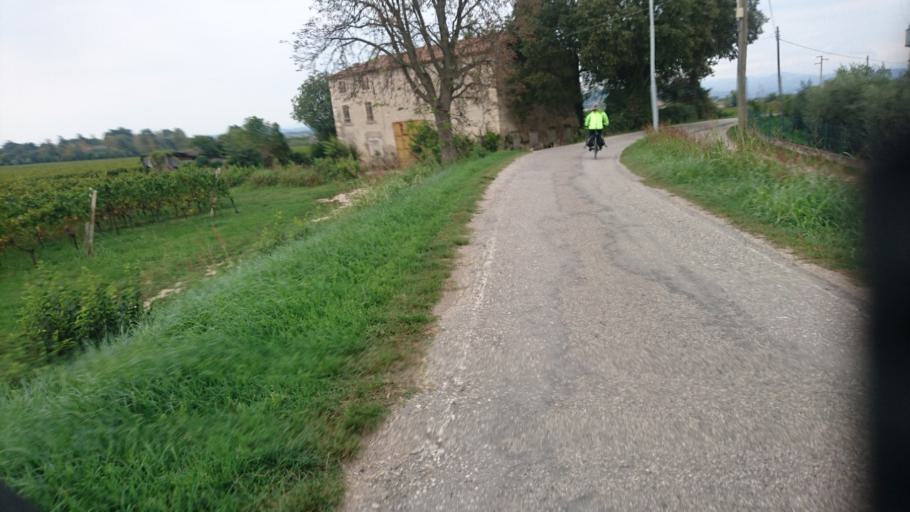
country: IT
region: Veneto
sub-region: Provincia di Verona
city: Caldierino-Rota
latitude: 45.4042
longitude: 11.1420
